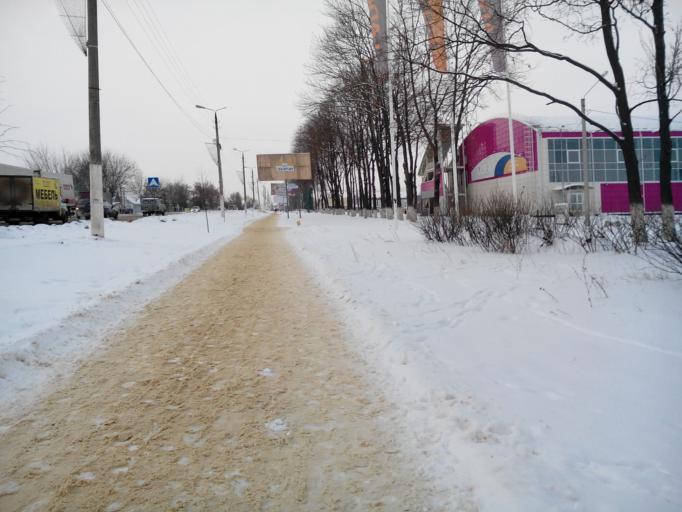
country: RU
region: Tula
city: Yefremov
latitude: 53.1466
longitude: 38.0941
